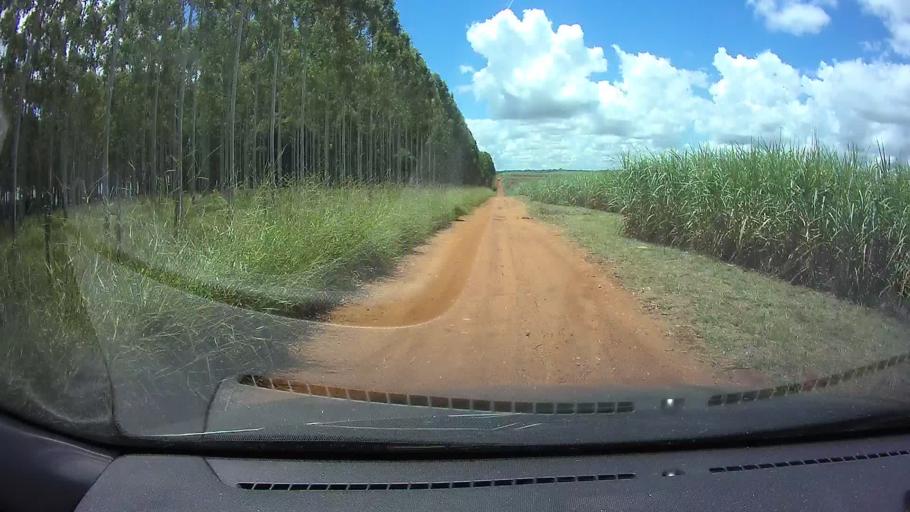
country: PY
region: Paraguari
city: La Colmena
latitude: -25.9632
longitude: -56.7320
